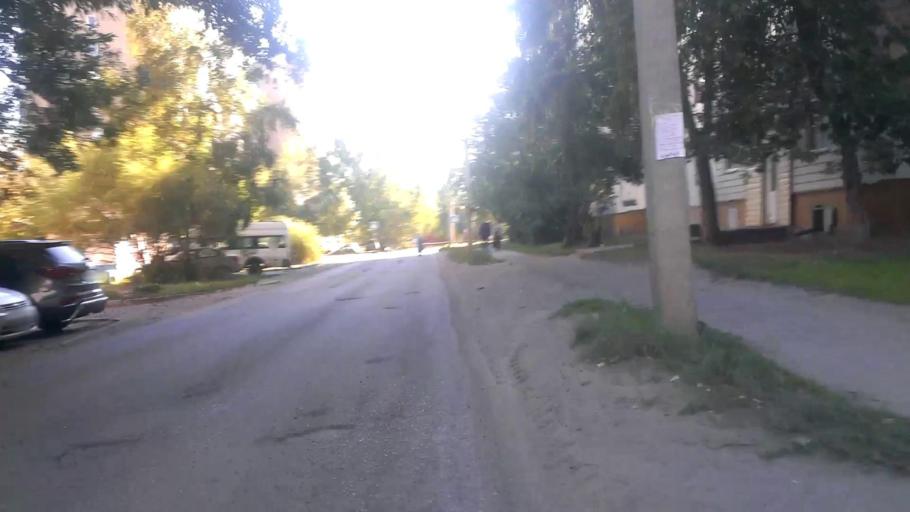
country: RU
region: Altai Krai
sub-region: Gorod Barnaulskiy
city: Barnaul
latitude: 53.3732
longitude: 83.6912
